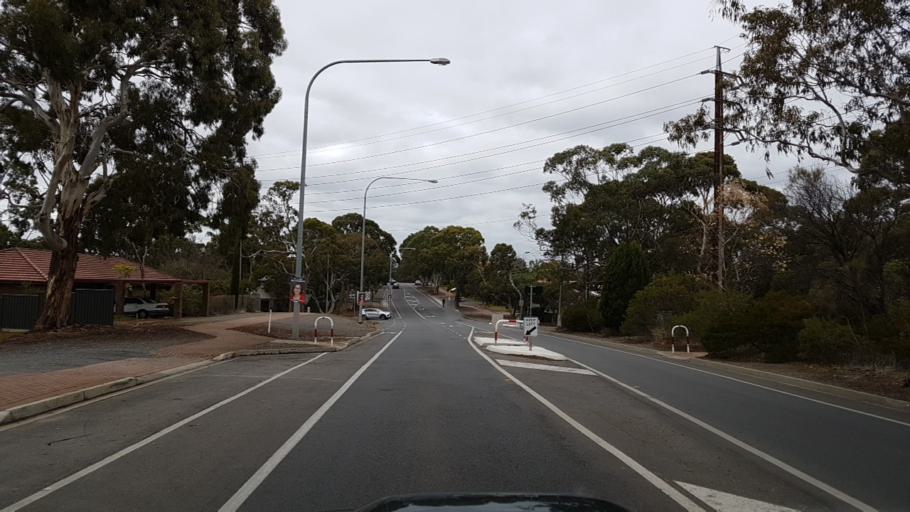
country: AU
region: South Australia
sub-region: Onkaparinga
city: Bedford Park
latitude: -35.0505
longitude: 138.5782
